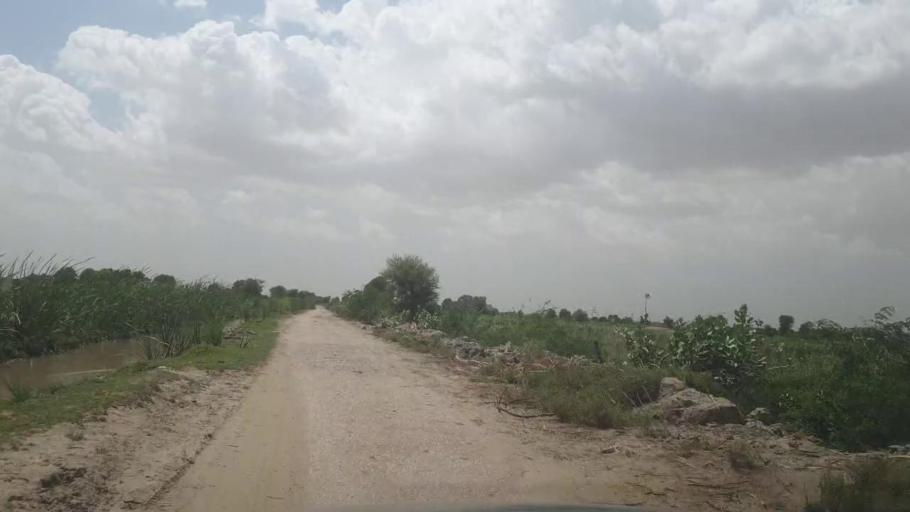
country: PK
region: Sindh
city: Kot Diji
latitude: 27.2352
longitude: 69.0152
